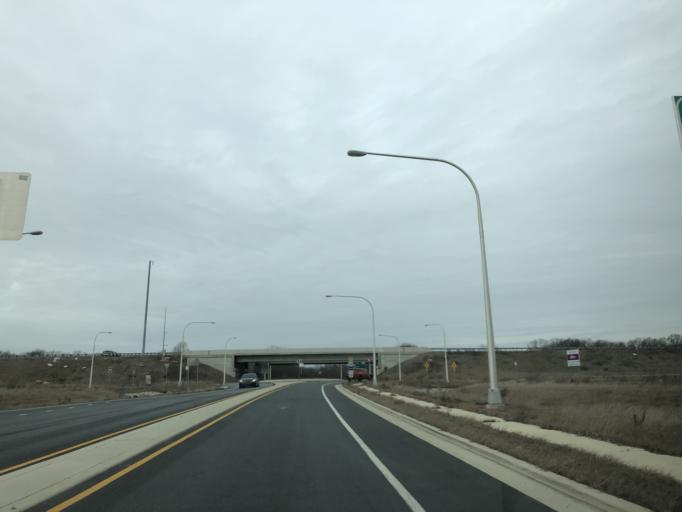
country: US
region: Delaware
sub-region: New Castle County
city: Middletown
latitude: 39.4838
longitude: -75.7201
